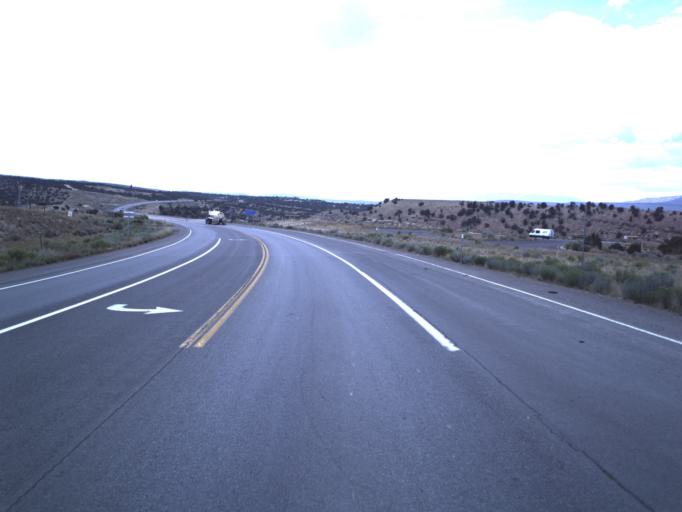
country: US
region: Utah
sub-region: Duchesne County
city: Duchesne
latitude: 40.1723
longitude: -110.4900
